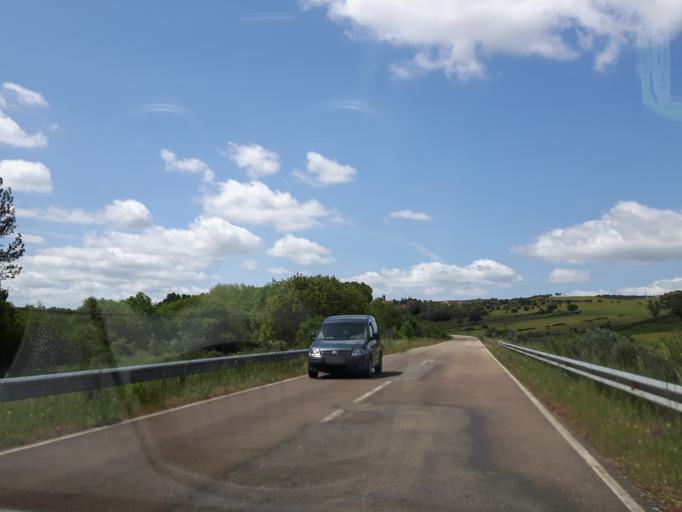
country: ES
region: Castille and Leon
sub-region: Provincia de Salamanca
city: Aldea del Obispo
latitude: 40.7185
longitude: -6.7824
